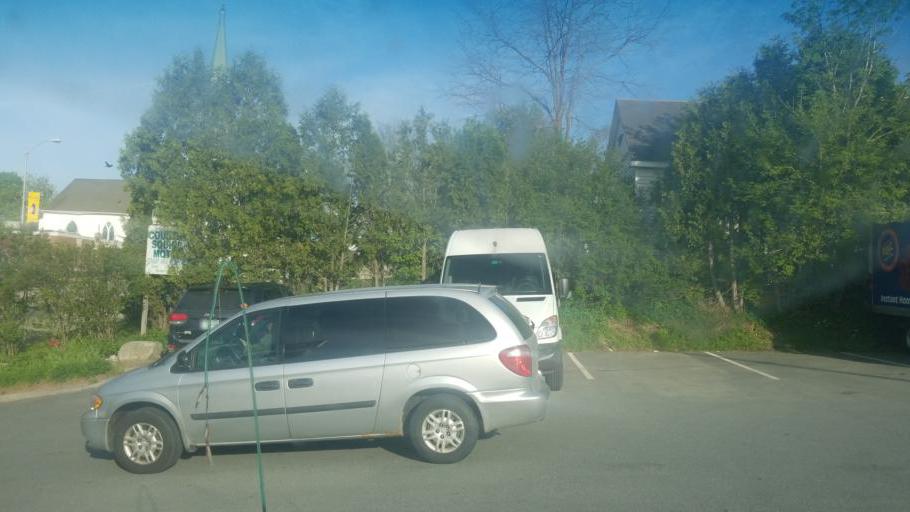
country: US
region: New Hampshire
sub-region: Grafton County
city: Littleton
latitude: 44.3075
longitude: -71.7759
